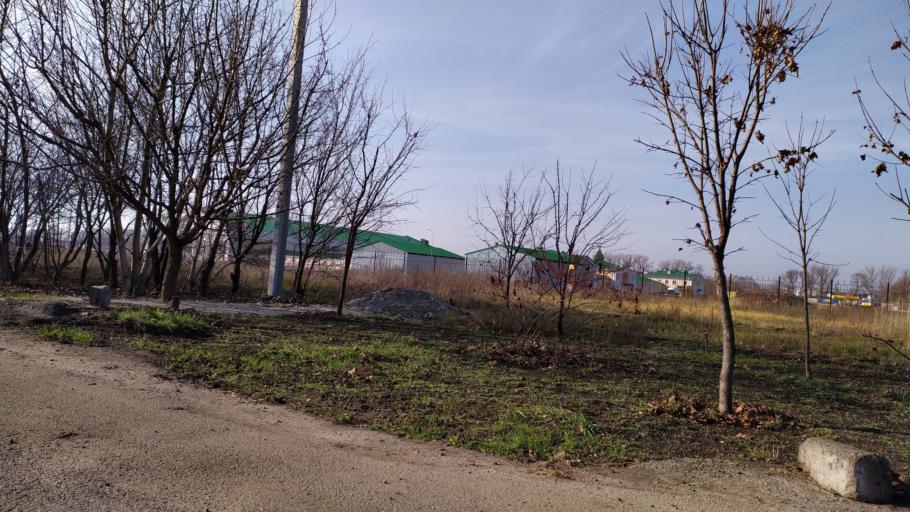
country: RU
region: Kursk
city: Kursk
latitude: 51.6430
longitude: 36.1318
